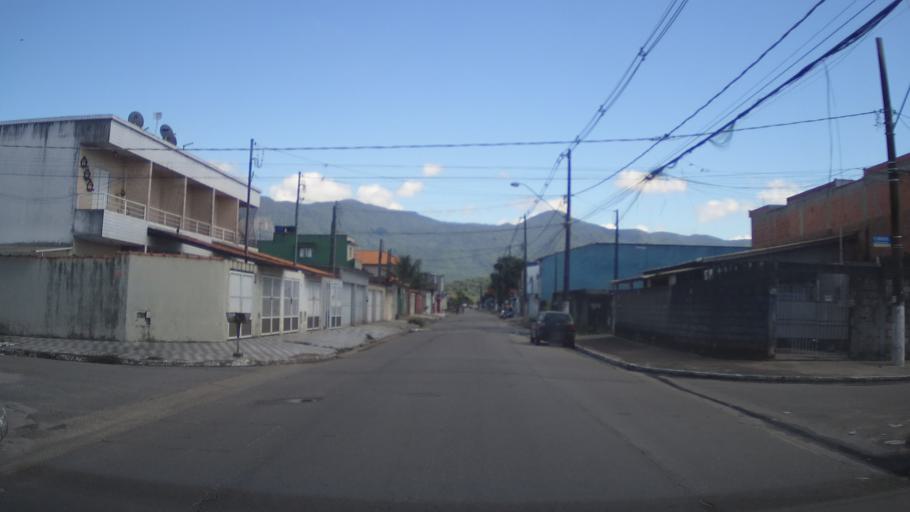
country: BR
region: Sao Paulo
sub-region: Mongagua
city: Mongagua
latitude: -24.0354
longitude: -46.5217
